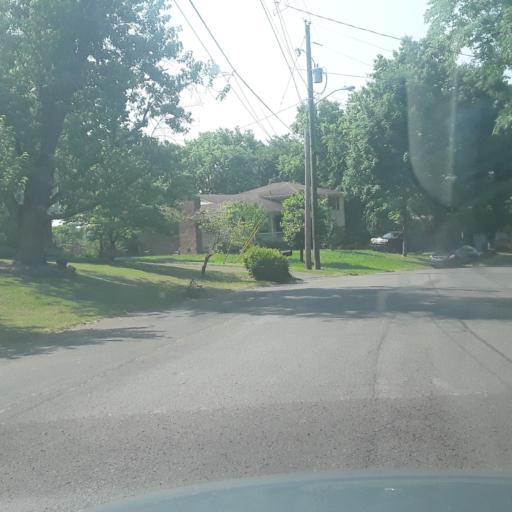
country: US
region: Tennessee
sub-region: Williamson County
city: Brentwood Estates
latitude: 36.0363
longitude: -86.7088
